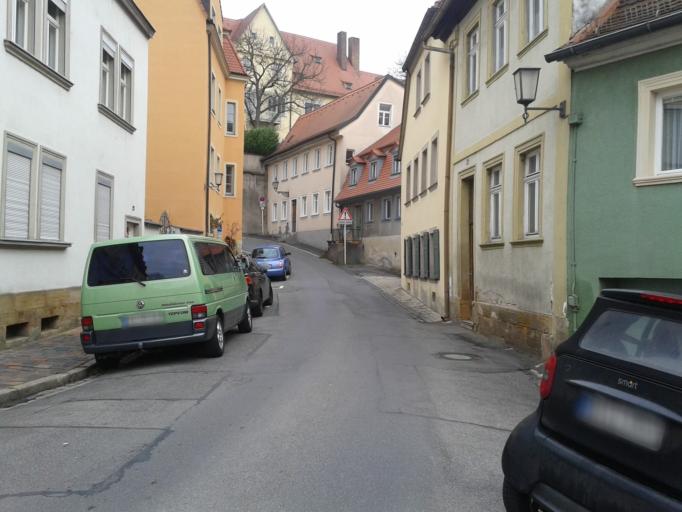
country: DE
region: Bavaria
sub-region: Upper Franconia
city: Bamberg
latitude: 49.8896
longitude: 10.8801
